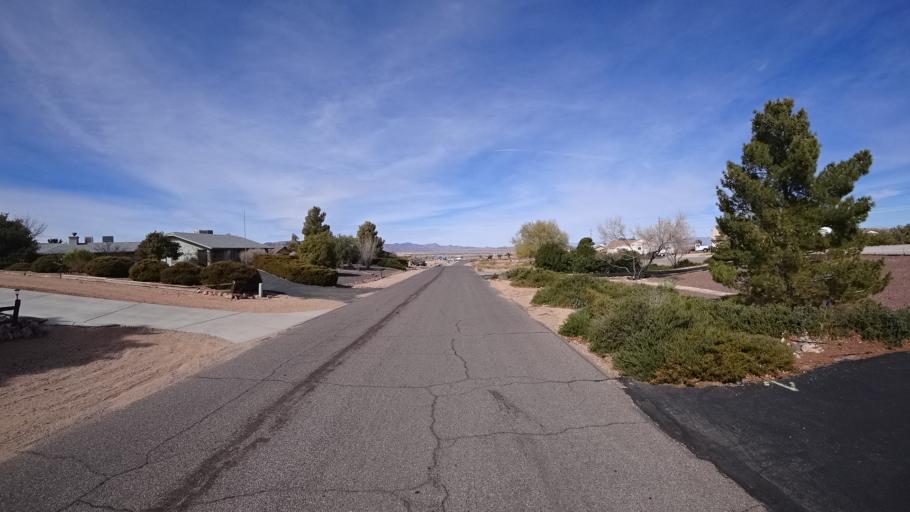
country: US
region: Arizona
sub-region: Mohave County
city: Kingman
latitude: 35.1932
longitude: -113.9877
